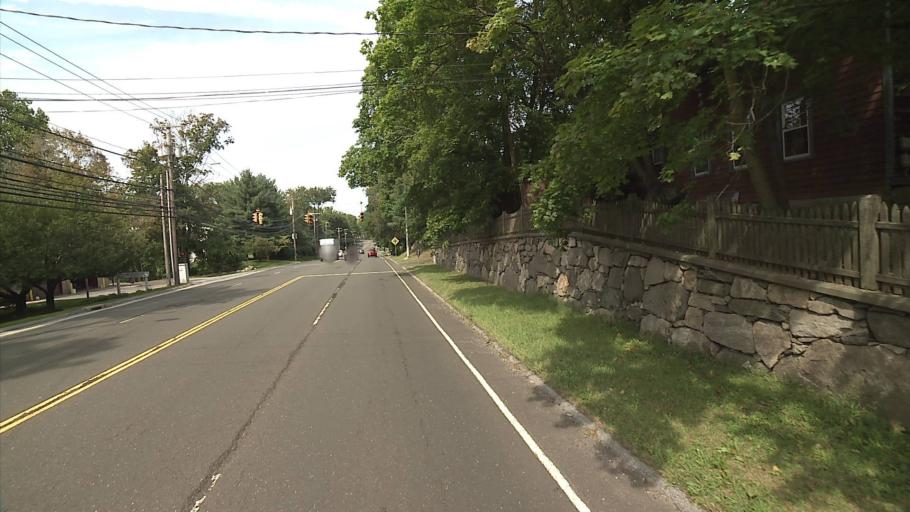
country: US
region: Connecticut
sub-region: Fairfield County
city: Stamford
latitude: 41.0924
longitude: -73.5616
